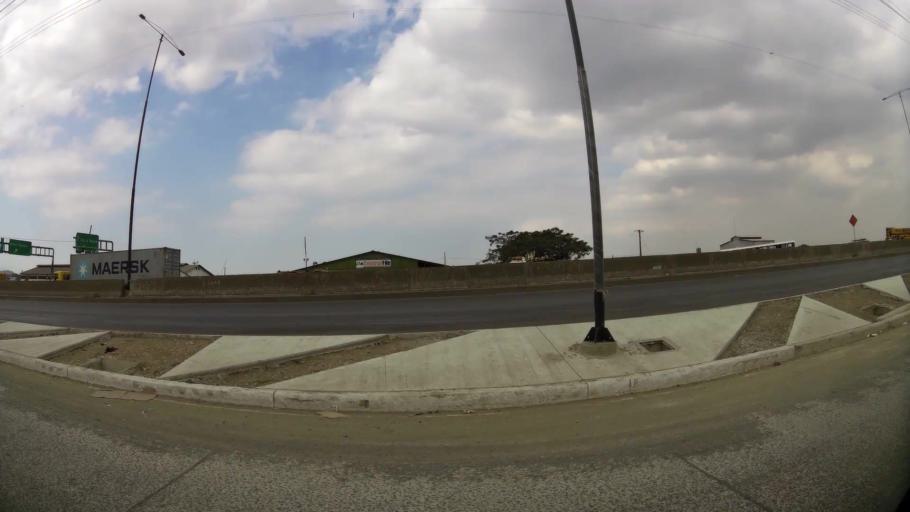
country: EC
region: Guayas
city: Santa Lucia
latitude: -2.1079
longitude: -79.9480
